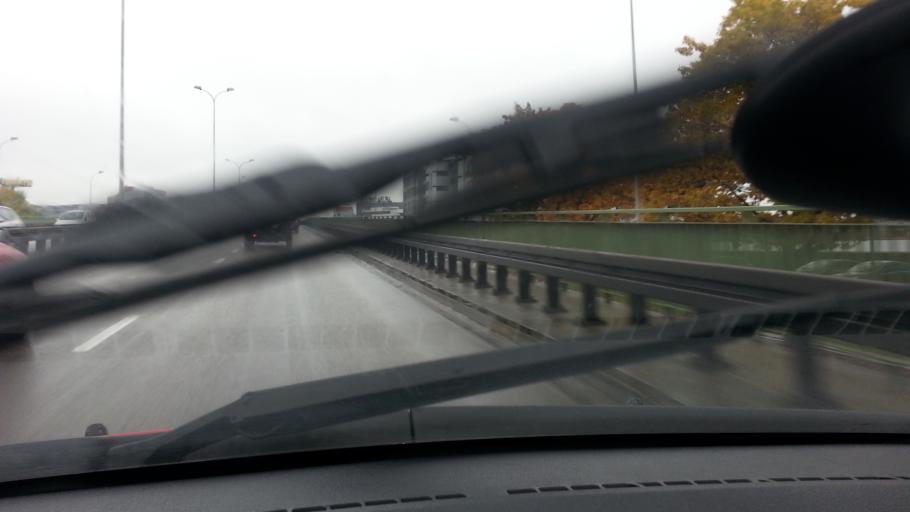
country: PL
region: Masovian Voivodeship
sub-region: Warszawa
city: Wlochy
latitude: 52.1997
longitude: 20.9341
